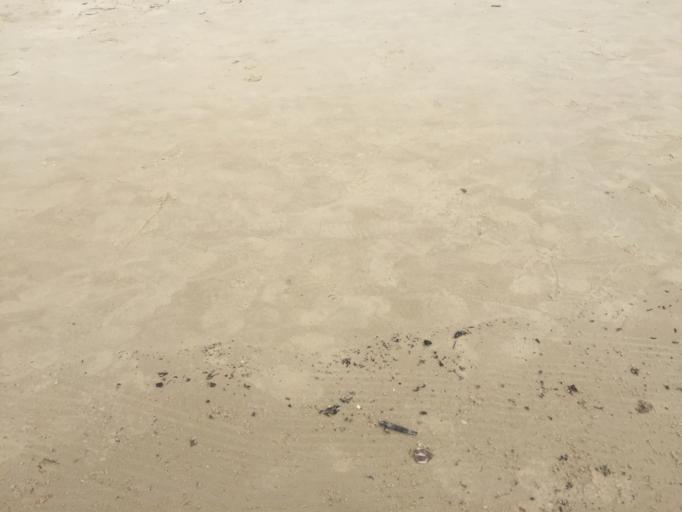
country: TH
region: Rayong
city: Rayong
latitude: 12.5638
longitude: 101.4575
